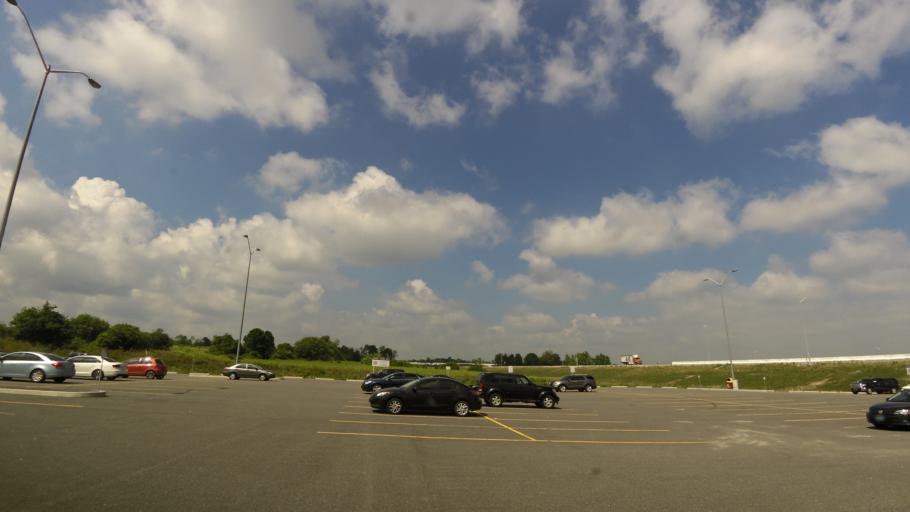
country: CA
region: Ontario
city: Ajax
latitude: 43.9424
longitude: -79.0090
